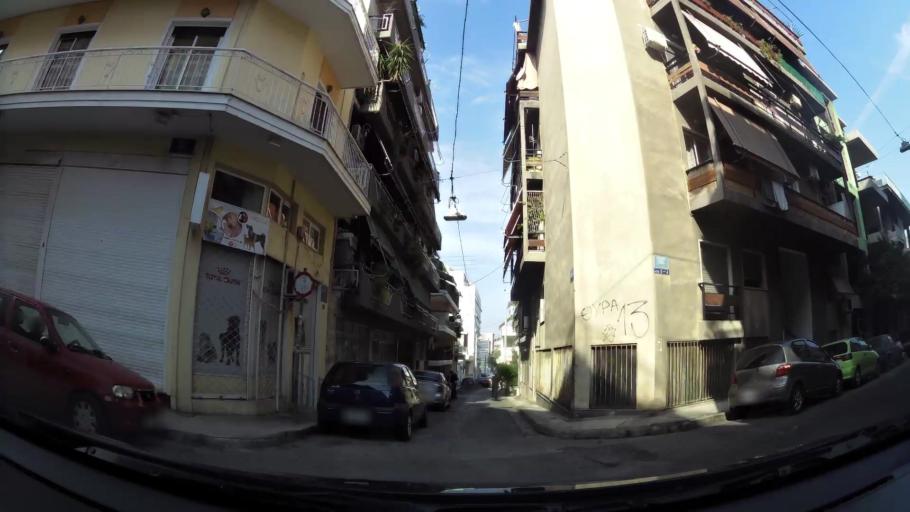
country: GR
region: Attica
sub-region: Nomarchia Athinas
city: Athens
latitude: 37.9729
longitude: 23.7093
